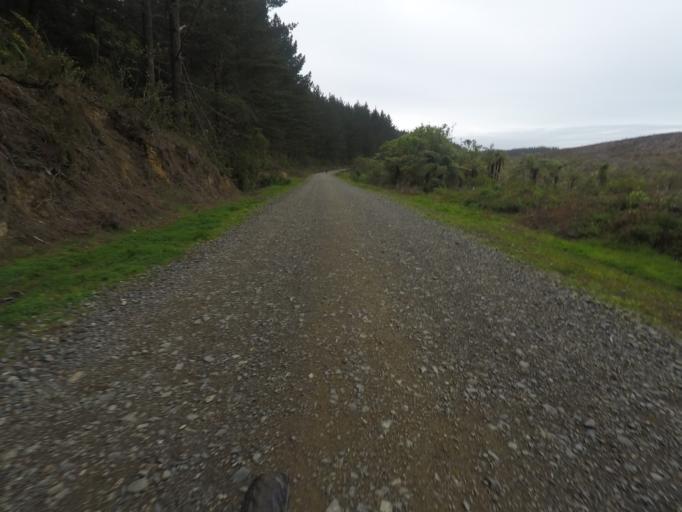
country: NZ
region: Auckland
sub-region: Auckland
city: Muriwai Beach
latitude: -36.7506
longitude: 174.5752
